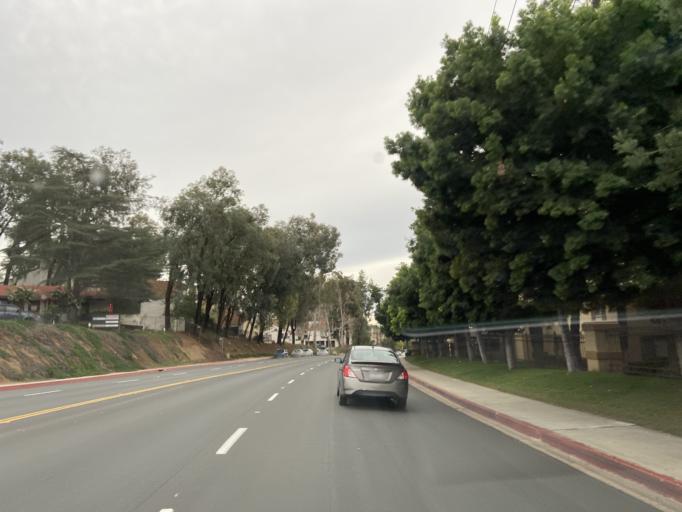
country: US
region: California
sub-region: San Diego County
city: Escondido
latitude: 33.1009
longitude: -117.0707
